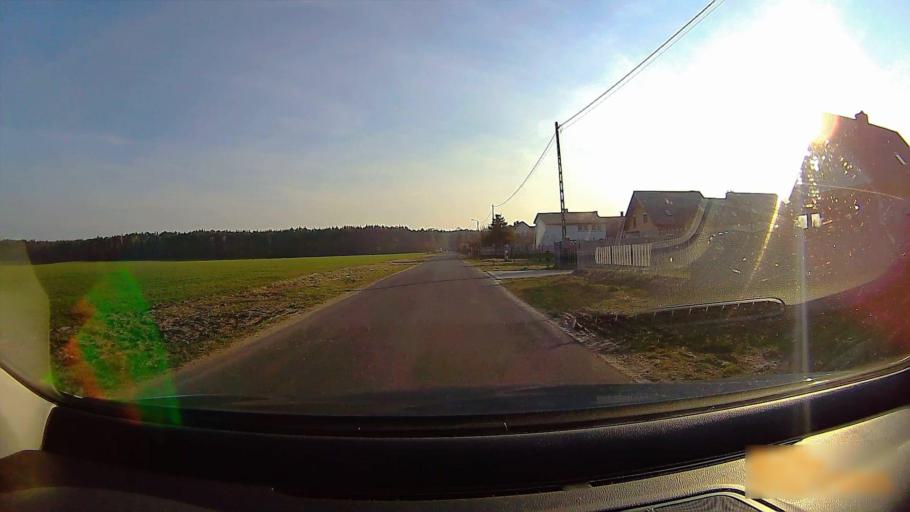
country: PL
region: Greater Poland Voivodeship
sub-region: Konin
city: Konin
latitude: 52.1802
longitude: 18.3008
